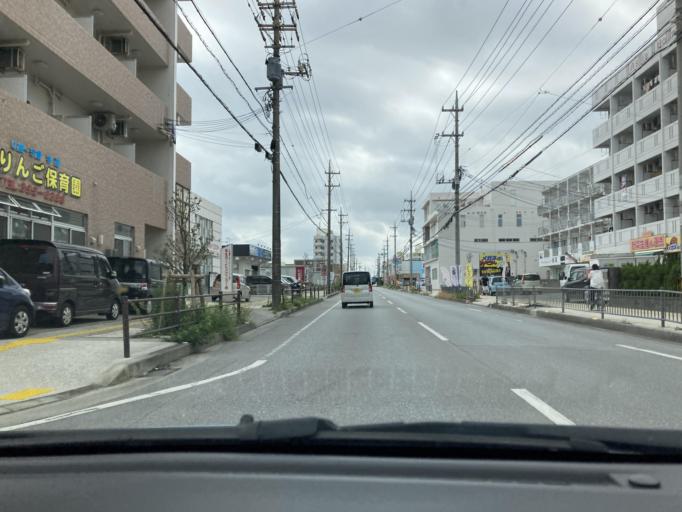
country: JP
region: Okinawa
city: Ginowan
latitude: 26.2459
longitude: 127.7697
